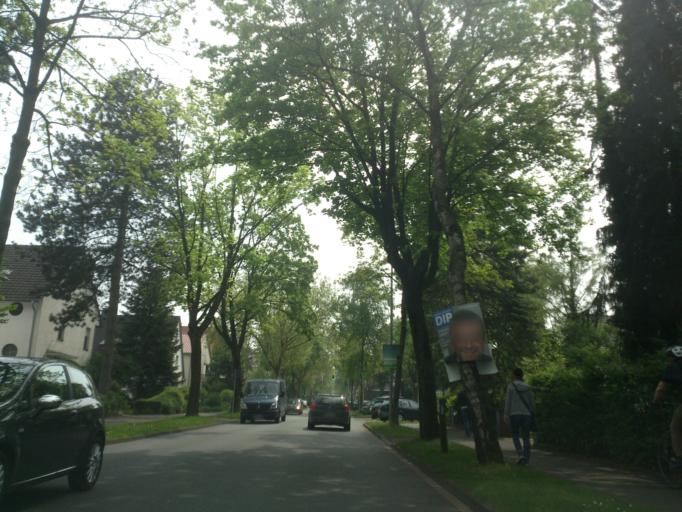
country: DE
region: North Rhine-Westphalia
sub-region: Regierungsbezirk Detmold
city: Paderborn
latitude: 51.7102
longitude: 8.7611
